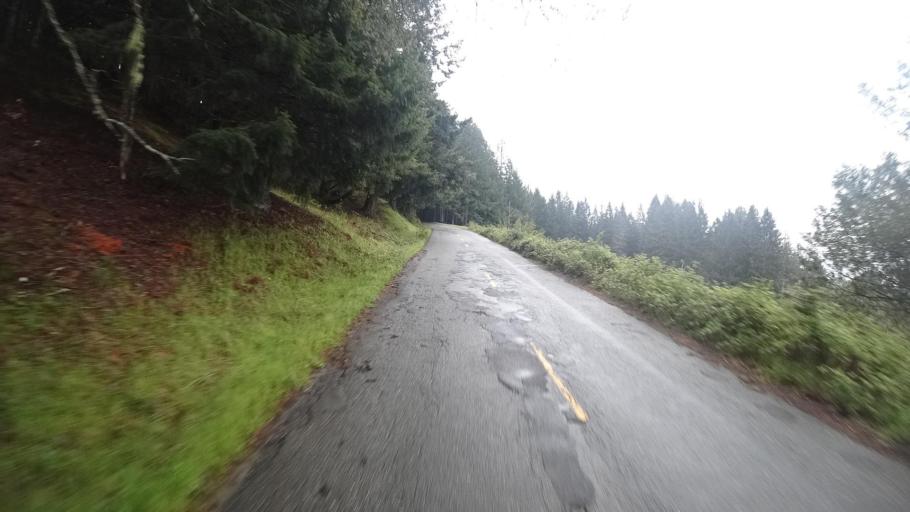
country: US
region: California
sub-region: Humboldt County
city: Westhaven-Moonstone
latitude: 41.2244
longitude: -123.9623
